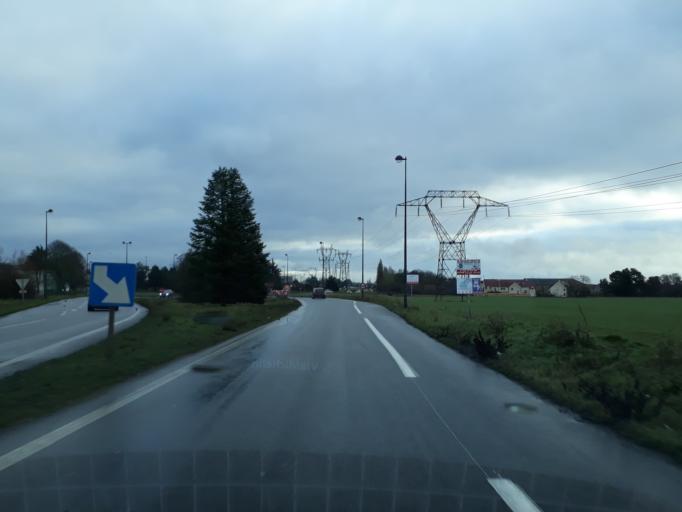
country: FR
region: Ile-de-France
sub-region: Departement de l'Essonne
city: Les Ulis
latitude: 48.6744
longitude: 2.1631
